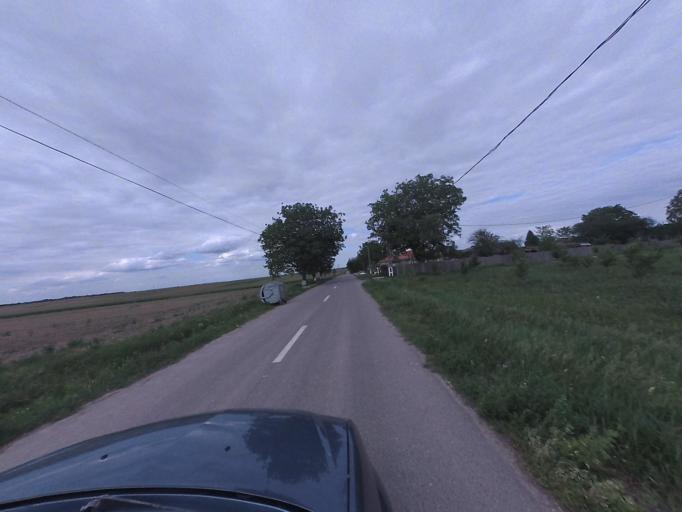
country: RO
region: Neamt
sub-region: Comuna Trifesti
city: Miron Costin
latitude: 46.9570
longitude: 26.8129
